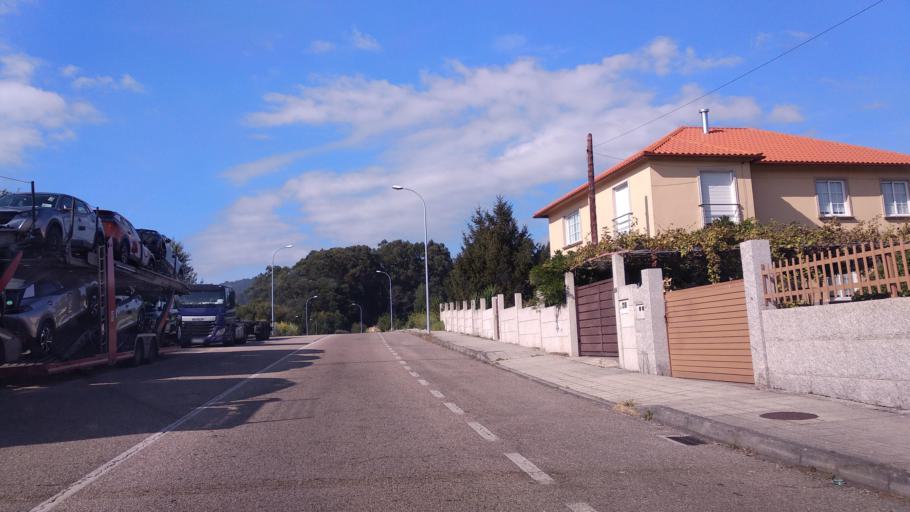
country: ES
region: Galicia
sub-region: Provincia de Pontevedra
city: Cangas
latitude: 42.2639
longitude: -8.7655
